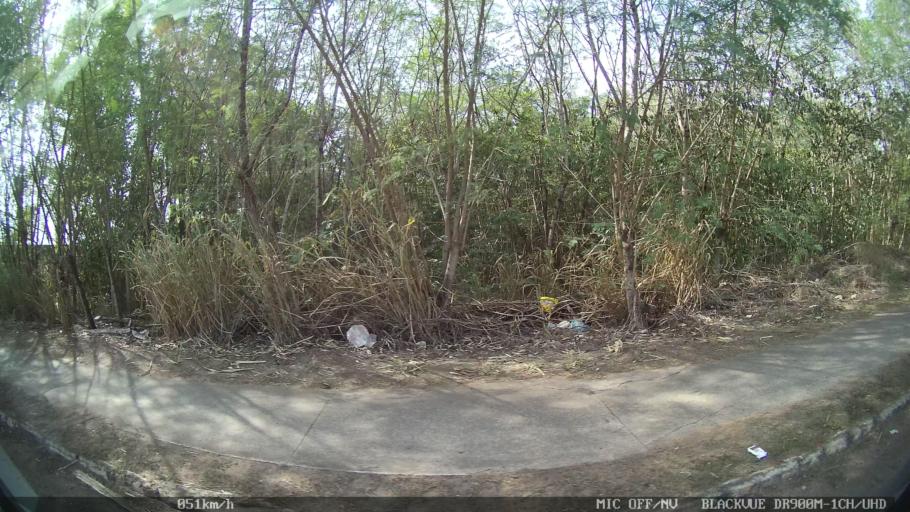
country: BR
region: Sao Paulo
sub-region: Piracicaba
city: Piracicaba
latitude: -22.7019
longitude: -47.6757
